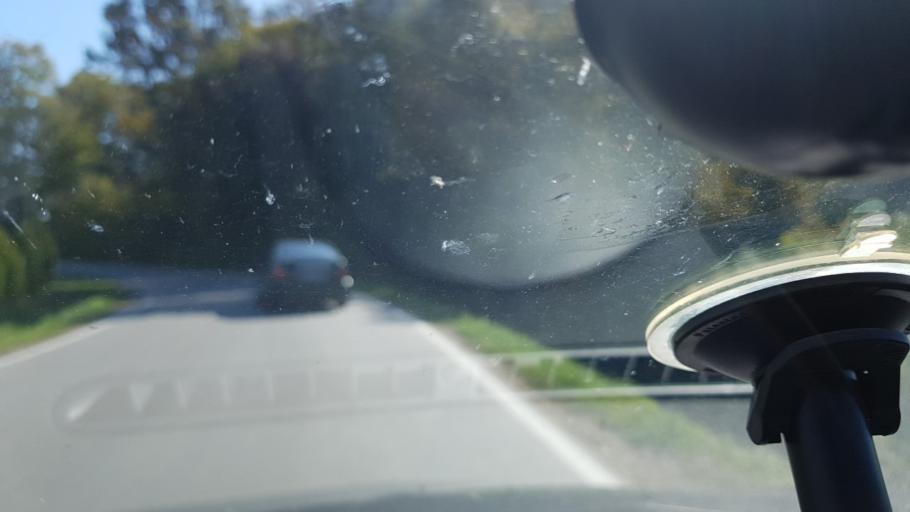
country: HR
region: Zagrebacka
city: Lupoglav
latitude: 45.7216
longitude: 16.3090
